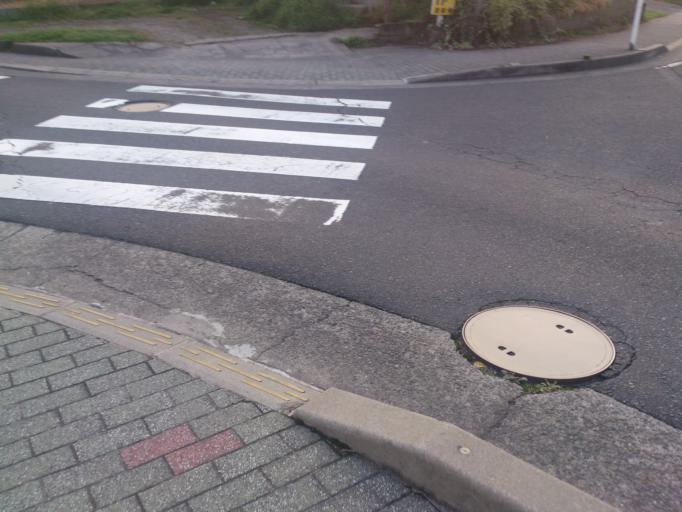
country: JP
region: Kagoshima
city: Kagoshima-shi
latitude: 31.5789
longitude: 130.5103
